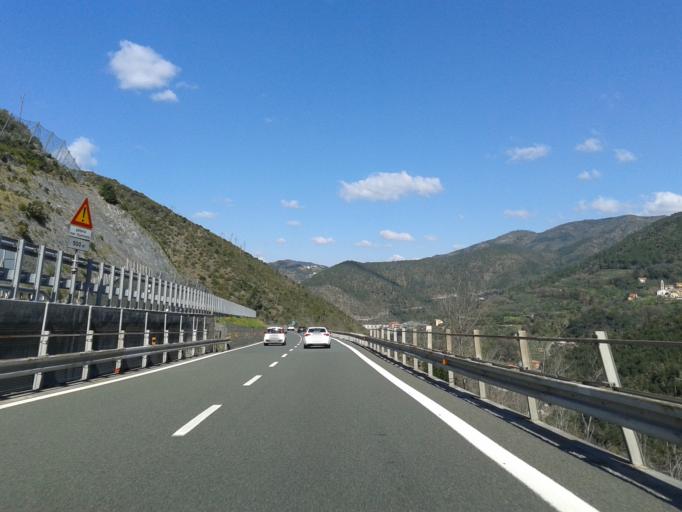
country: IT
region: Liguria
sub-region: Provincia di Genova
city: Moneglia
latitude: 44.2656
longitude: 9.4814
